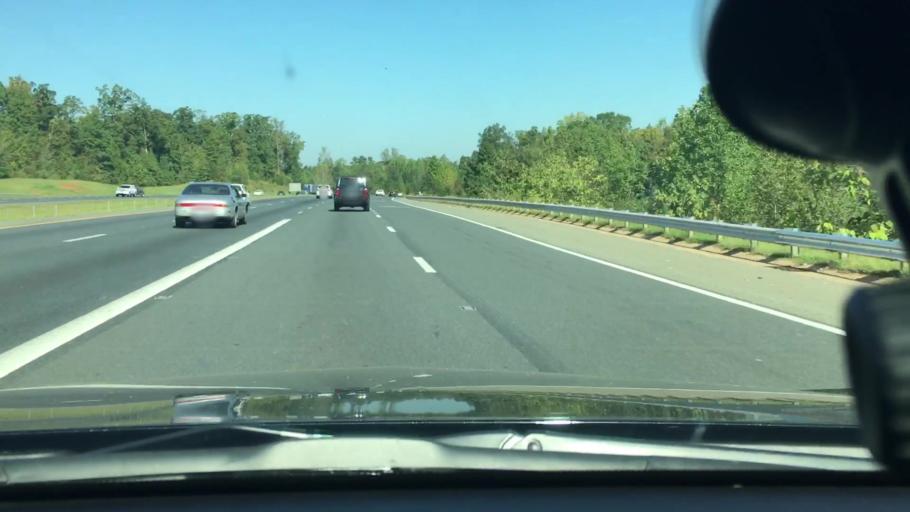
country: US
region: North Carolina
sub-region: Mecklenburg County
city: Mint Hill
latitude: 35.2246
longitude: -80.6523
